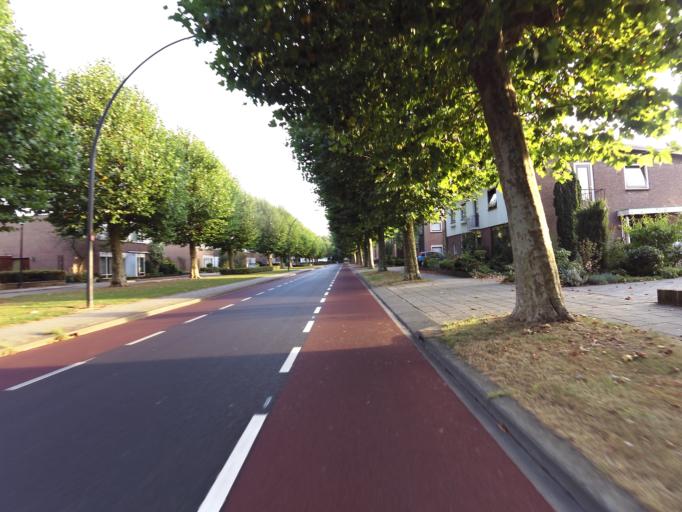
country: NL
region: Gelderland
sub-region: Gemeente Zevenaar
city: Zevenaar
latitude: 51.9257
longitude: 6.0713
